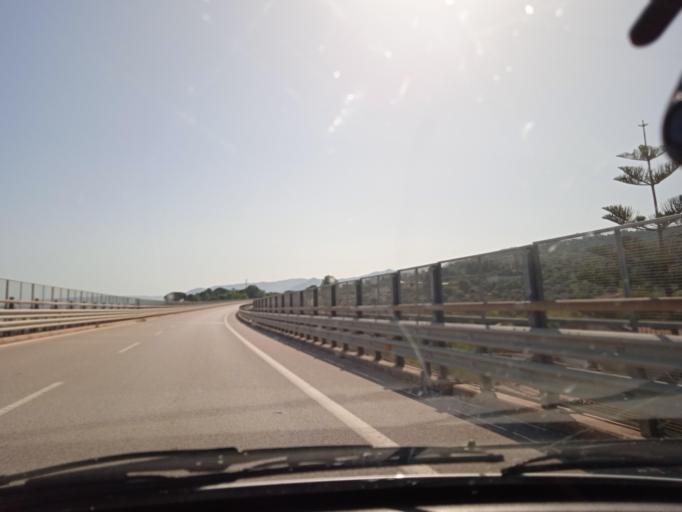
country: IT
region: Sicily
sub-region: Messina
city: Acquedolci
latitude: 38.0520
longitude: 14.5899
